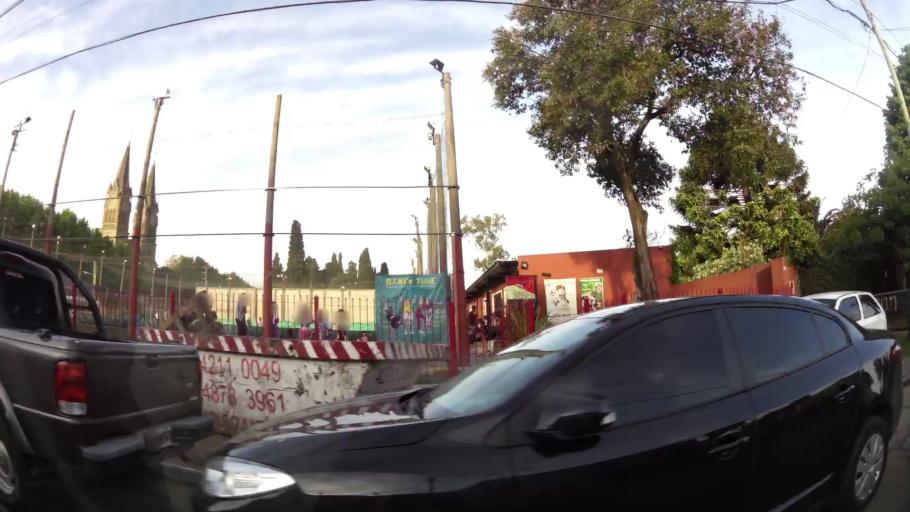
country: AR
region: Buenos Aires
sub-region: Partido de Almirante Brown
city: Adrogue
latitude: -34.7902
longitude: -58.3535
